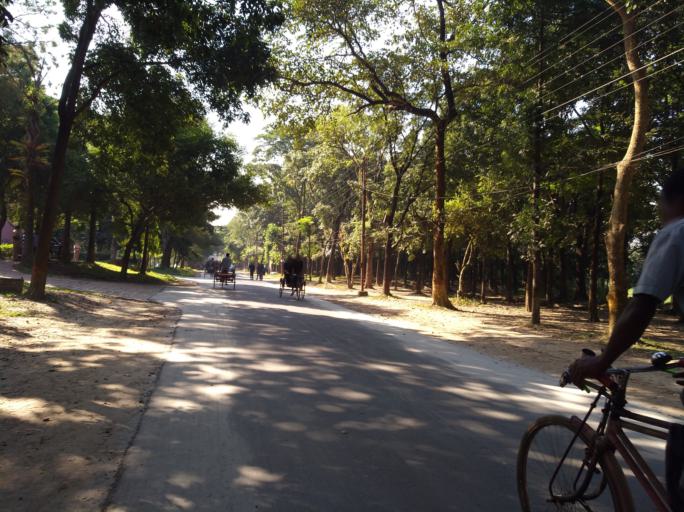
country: BD
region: Dhaka
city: Tungi
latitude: 23.8832
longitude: 90.2679
